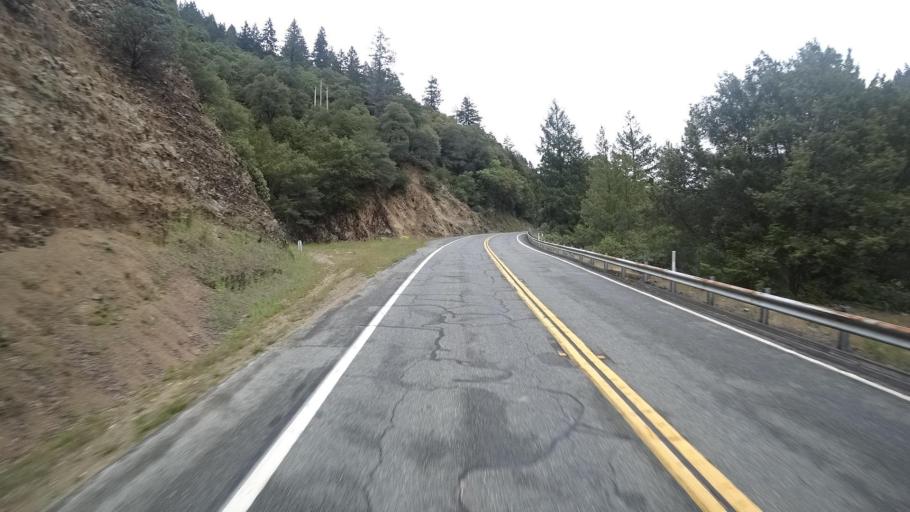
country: US
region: California
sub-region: Humboldt County
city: Willow Creek
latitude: 41.2594
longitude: -123.6183
